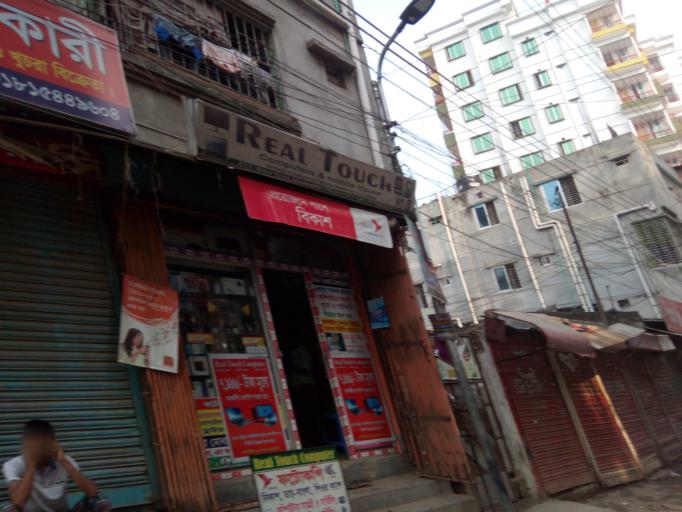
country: BD
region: Dhaka
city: Paltan
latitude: 23.7236
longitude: 90.4334
